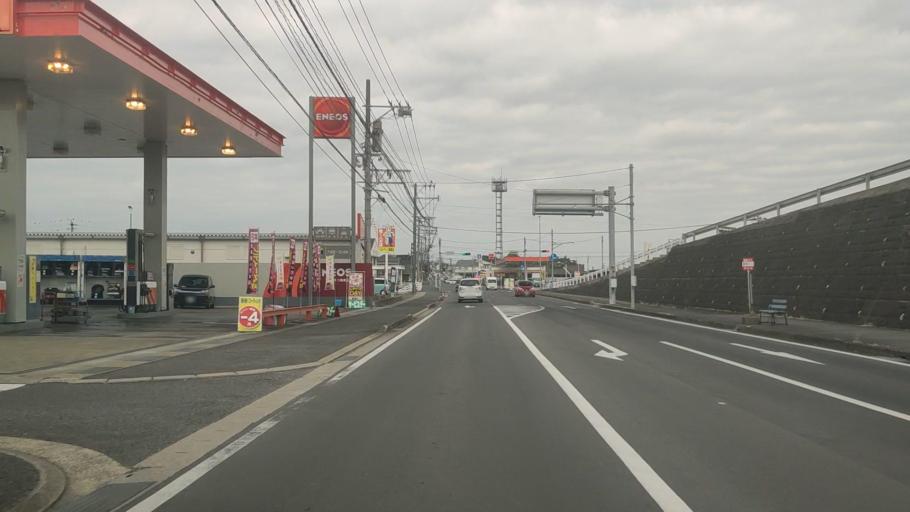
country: JP
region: Nagasaki
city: Shimabara
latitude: 32.8124
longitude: 130.3585
